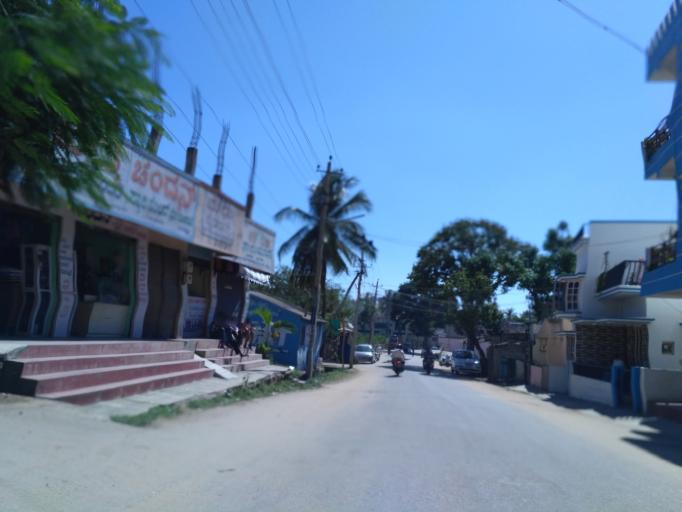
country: IN
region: Karnataka
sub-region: Hassan
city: Hassan
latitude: 13.0164
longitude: 76.0943
